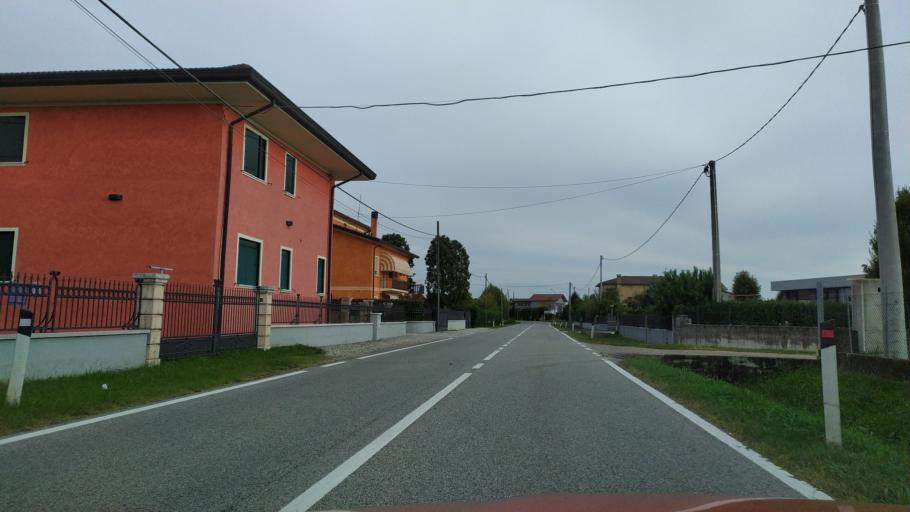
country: IT
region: Veneto
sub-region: Provincia di Padova
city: San Giorgio in Bosco
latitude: 45.5823
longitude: 11.7804
